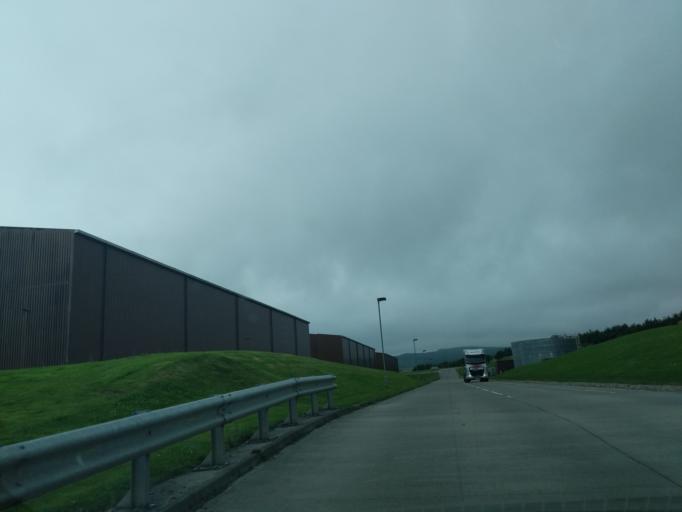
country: GB
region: Scotland
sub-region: Moray
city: Rothes
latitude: 57.4897
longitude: -3.2081
